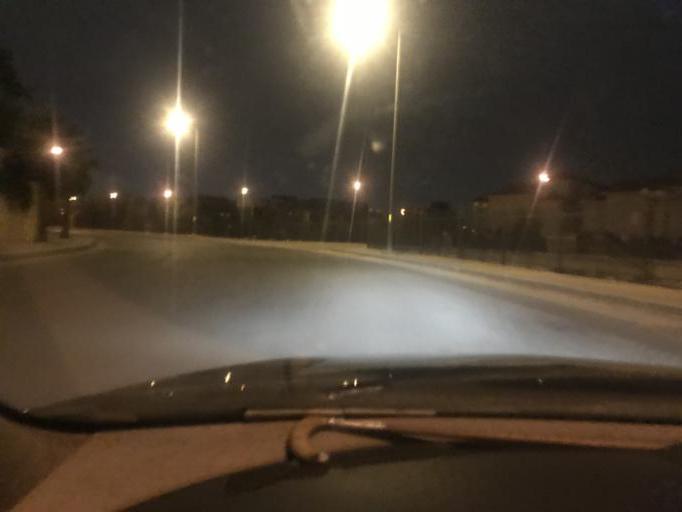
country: SA
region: Ar Riyad
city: Riyadh
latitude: 24.8074
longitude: 46.6772
